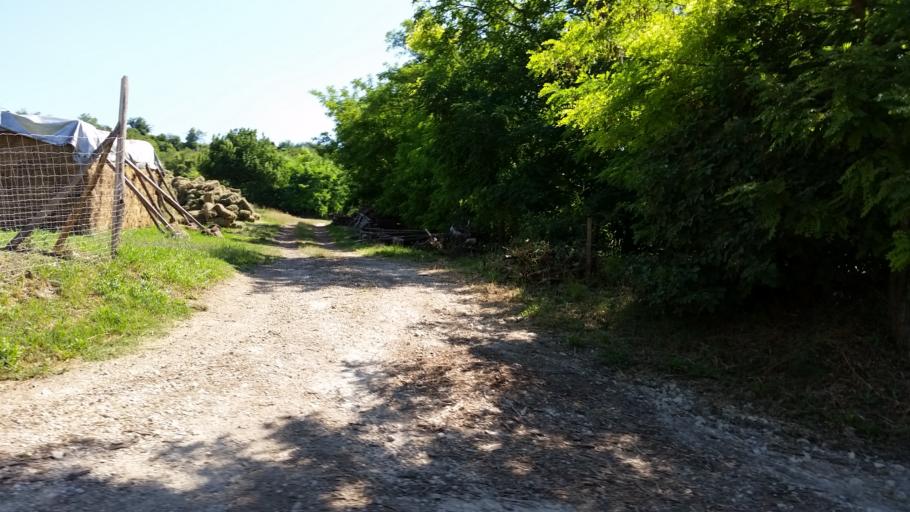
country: HU
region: Fejer
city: Many
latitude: 47.5306
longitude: 18.6045
